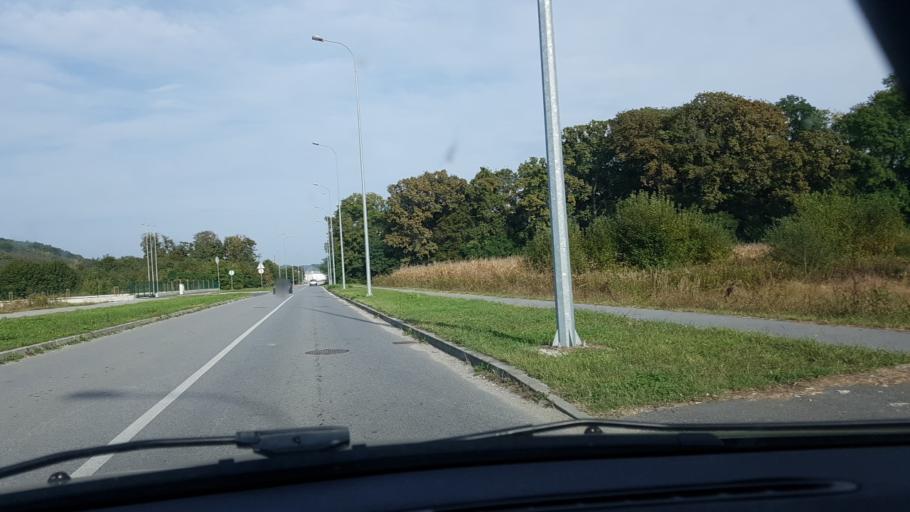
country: HR
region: Krapinsko-Zagorska
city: Zabok
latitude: 46.0153
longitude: 15.8853
